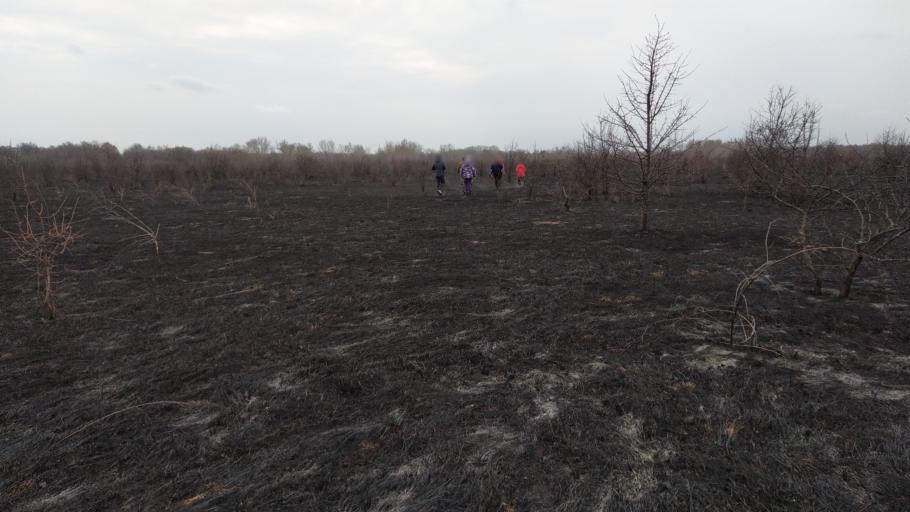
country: RU
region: Rostov
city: Semikarakorsk
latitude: 47.5450
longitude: 40.6843
